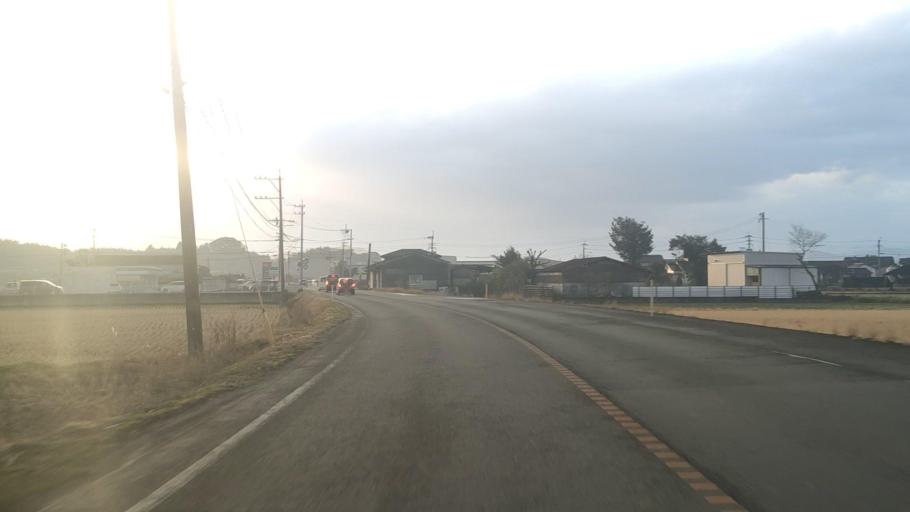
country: JP
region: Kumamoto
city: Uto
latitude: 32.7252
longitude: 130.7660
